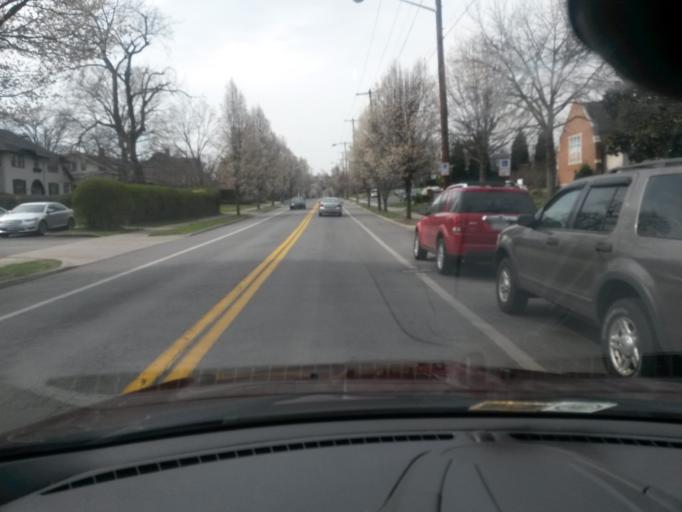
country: US
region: Virginia
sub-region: City of Roanoke
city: Roanoke
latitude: 37.2604
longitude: -79.9801
